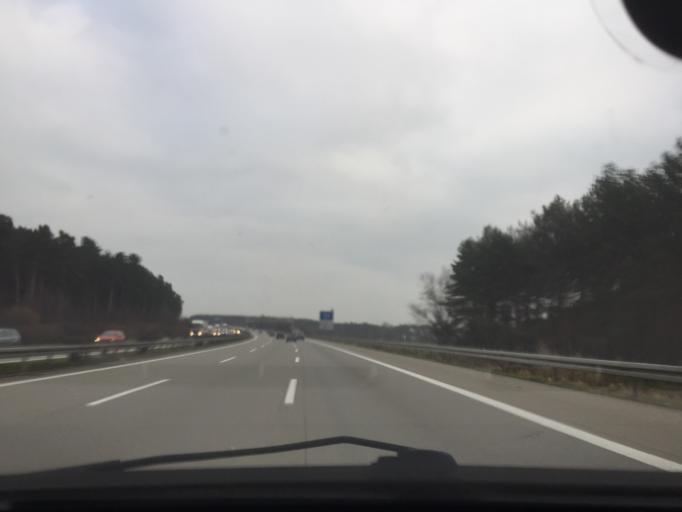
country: DE
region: Brandenburg
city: Ziesar
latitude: 52.2468
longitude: 12.2922
